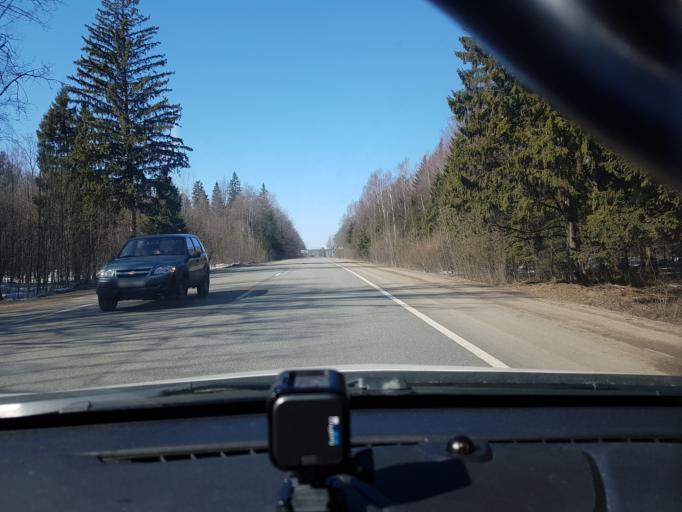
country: RU
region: Moskovskaya
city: Kostrovo
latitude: 55.9144
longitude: 36.6996
